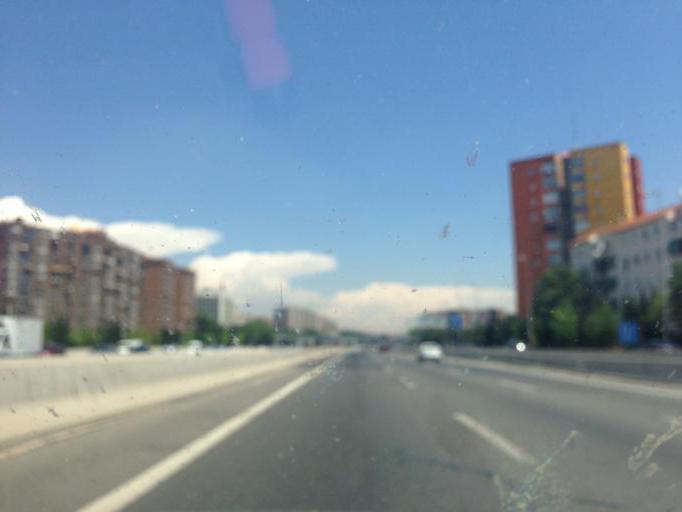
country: ES
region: Madrid
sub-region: Provincia de Madrid
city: Puente de Vallecas
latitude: 40.4020
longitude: -3.6672
